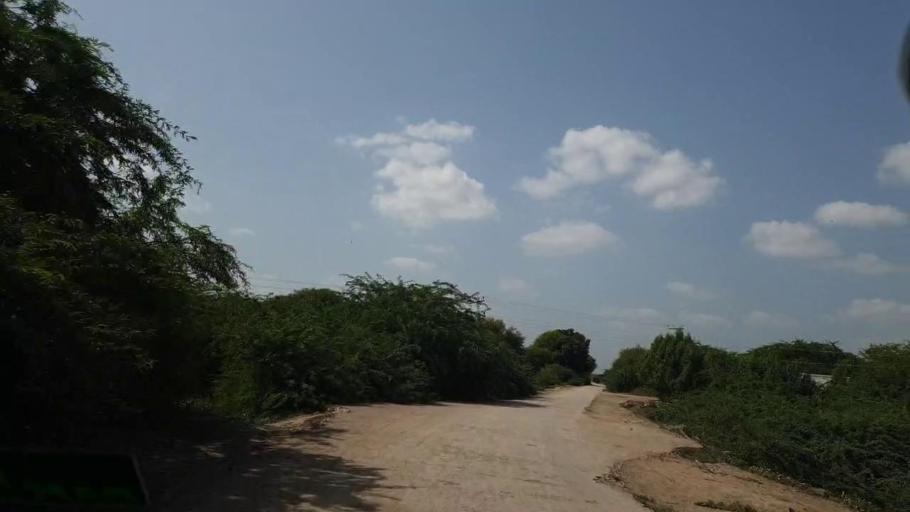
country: PK
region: Sindh
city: Naukot
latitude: 24.6435
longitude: 69.2251
